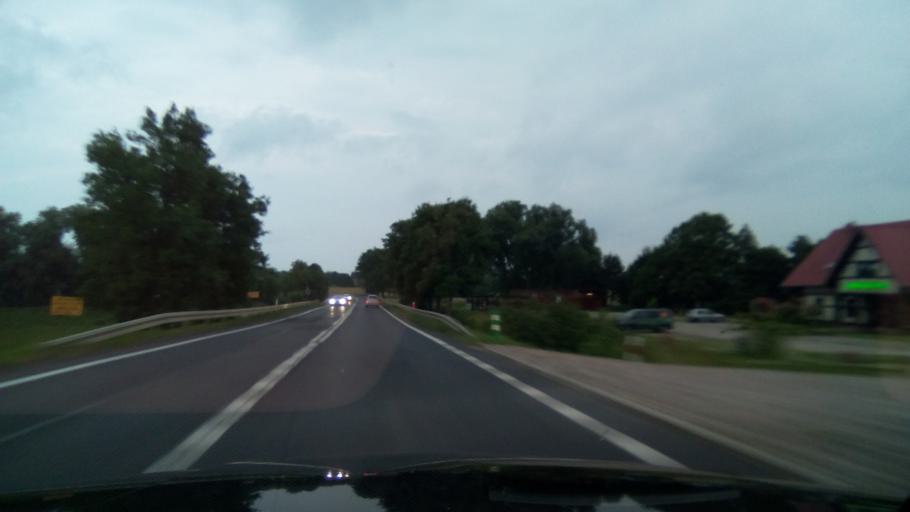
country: PL
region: Greater Poland Voivodeship
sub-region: Powiat gnieznienski
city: Lubowo
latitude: 52.5073
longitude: 17.3712
